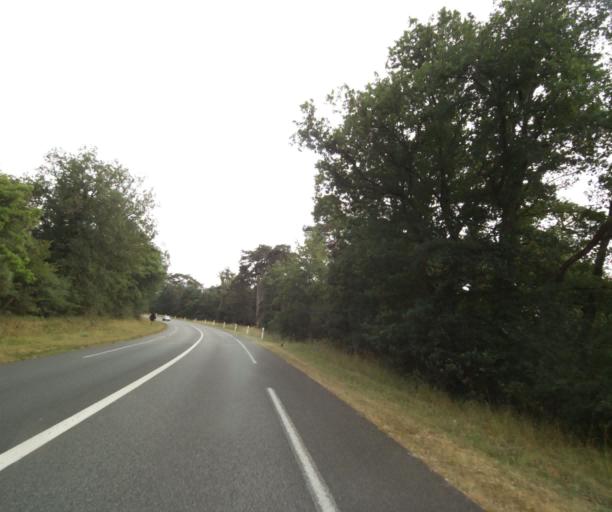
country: FR
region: Ile-de-France
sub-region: Departement de Seine-et-Marne
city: Bois-le-Roi
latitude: 48.4391
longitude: 2.6905
